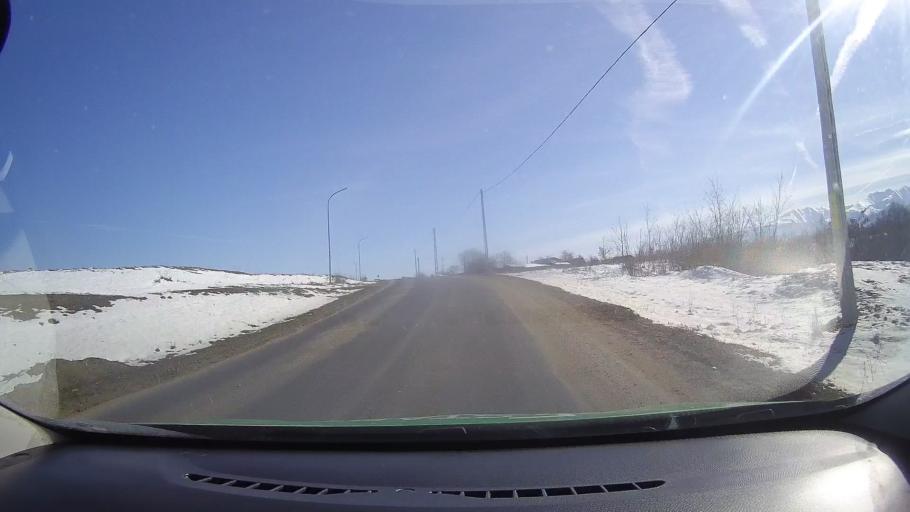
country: RO
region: Brasov
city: Ucea de Sus
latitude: 45.7543
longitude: 24.6880
